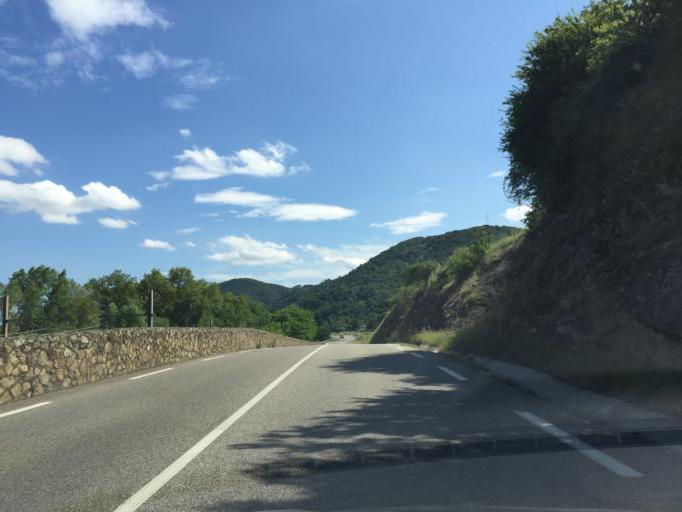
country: FR
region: Rhone-Alpes
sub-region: Departement de l'Ardeche
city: Saint-Jean-de-Muzols
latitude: 45.1269
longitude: 4.8012
